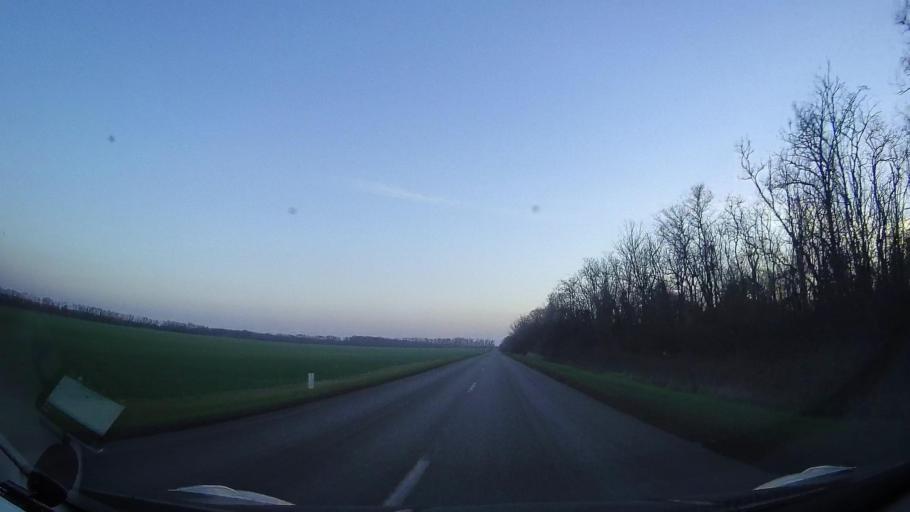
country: RU
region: Rostov
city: Zernograd
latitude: 46.9735
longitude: 40.3915
